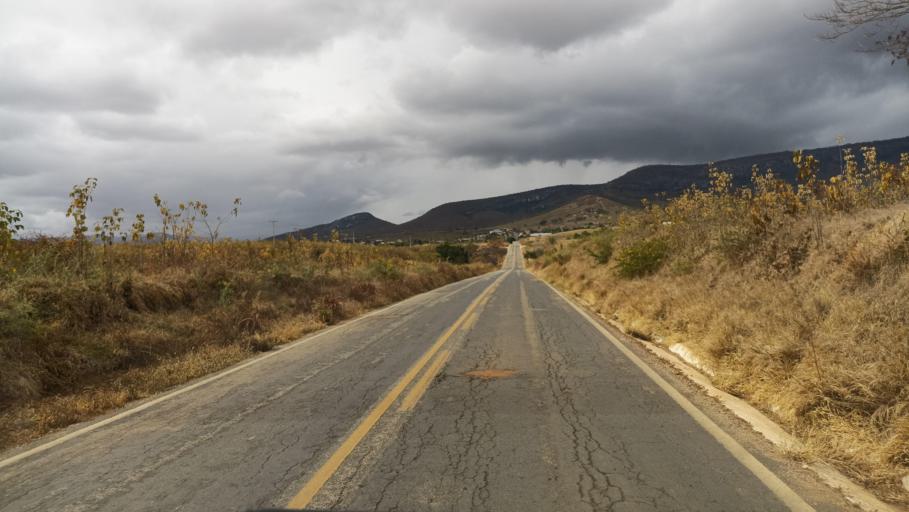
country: BR
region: Minas Gerais
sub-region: Itinga
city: Itinga
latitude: -16.6226
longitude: -41.7760
